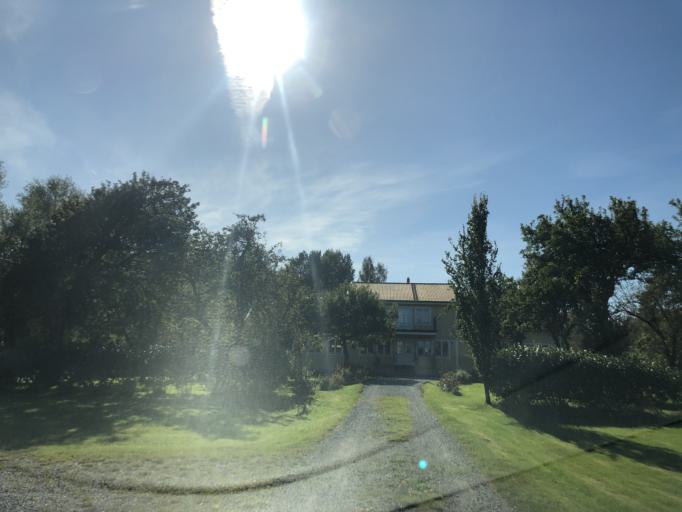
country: SE
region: Vaestra Goetaland
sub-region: Goteborg
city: Majorna
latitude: 57.7711
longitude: 11.9153
